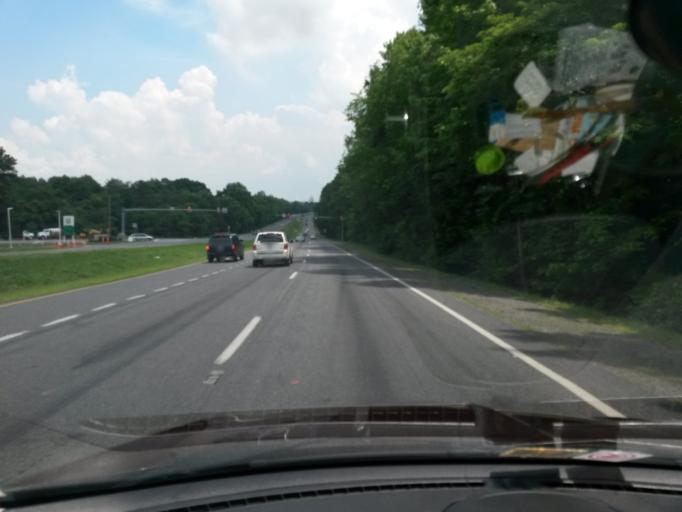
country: US
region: Virginia
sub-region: Chesterfield County
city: Enon
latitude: 37.3198
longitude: -77.3076
